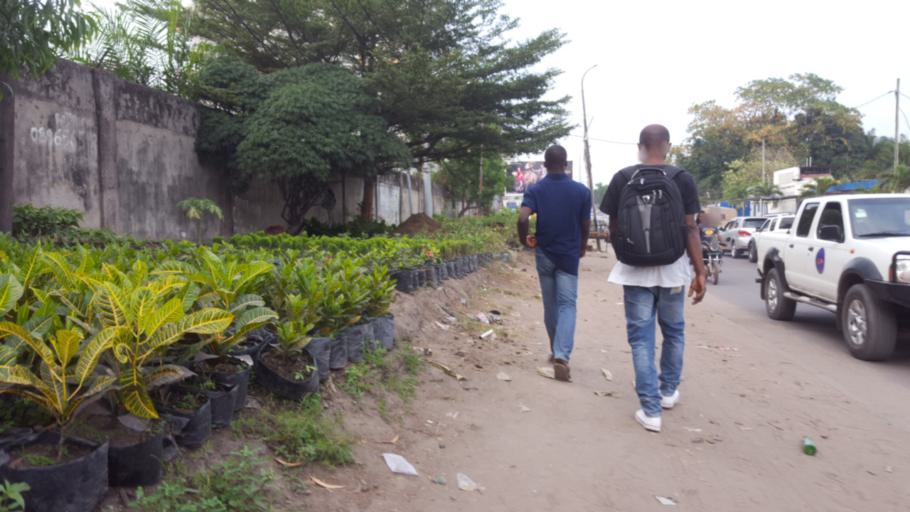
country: CD
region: Kinshasa
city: Kinshasa
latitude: -4.3244
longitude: 15.2774
